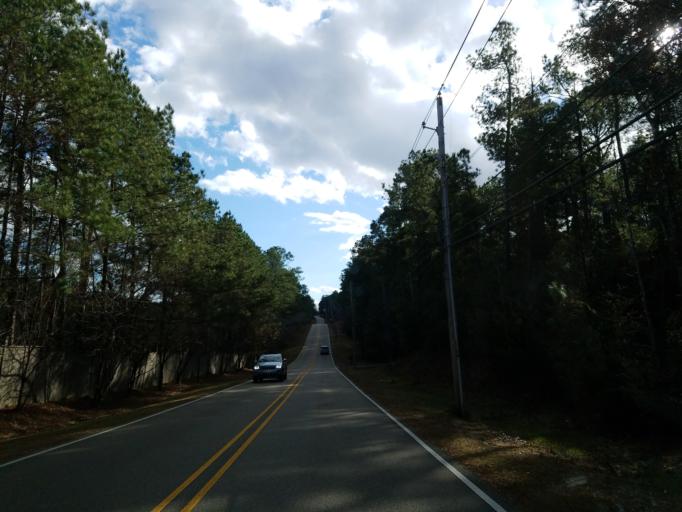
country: US
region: Mississippi
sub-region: Lamar County
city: West Hattiesburg
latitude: 31.2983
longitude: -89.3480
